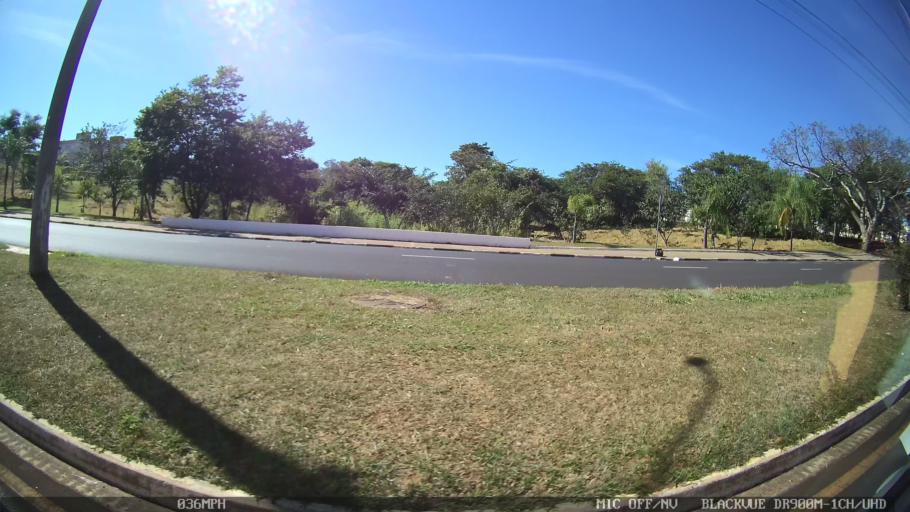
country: BR
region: Sao Paulo
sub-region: Franca
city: Franca
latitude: -20.5379
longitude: -47.3757
